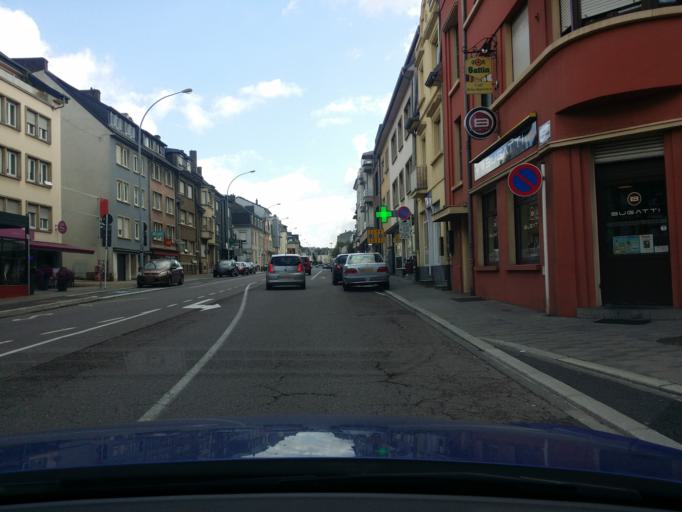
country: LU
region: Luxembourg
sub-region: Canton de Luxembourg
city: Luxembourg
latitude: 49.6064
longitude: 6.1068
